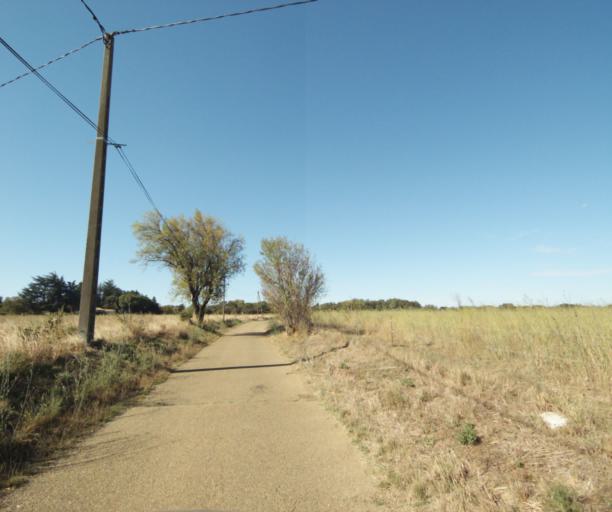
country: FR
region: Languedoc-Roussillon
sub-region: Departement du Gard
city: Bouillargues
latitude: 43.7932
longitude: 4.4195
